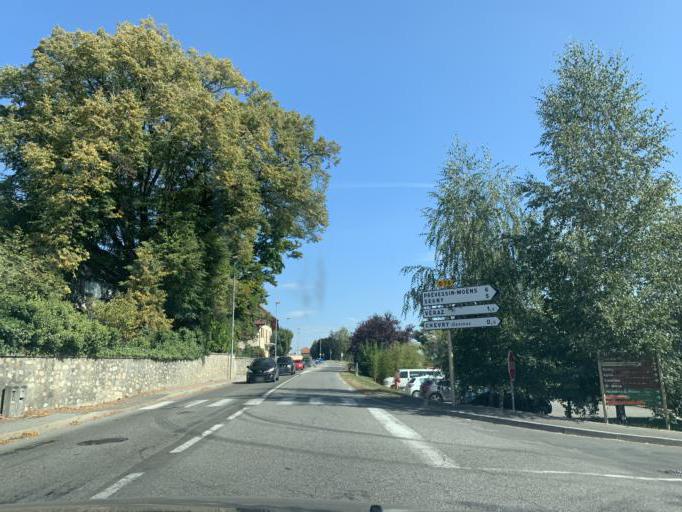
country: FR
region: Rhone-Alpes
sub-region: Departement de l'Ain
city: Chevry
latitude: 46.2803
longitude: 6.0372
